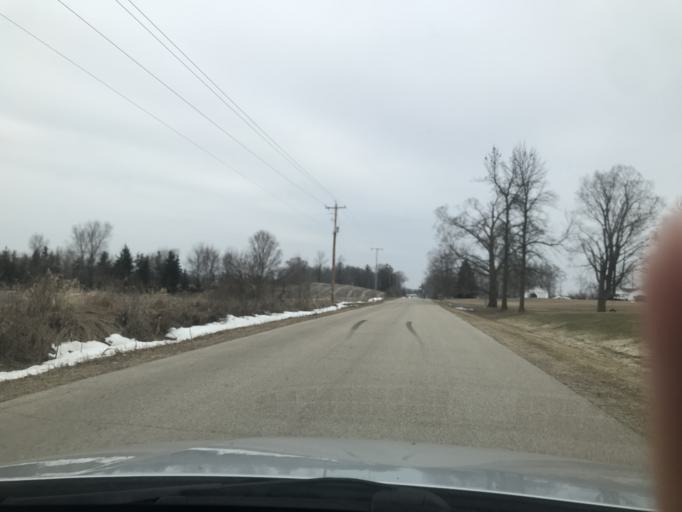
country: US
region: Wisconsin
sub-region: Marinette County
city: Peshtigo
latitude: 45.0408
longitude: -87.8592
